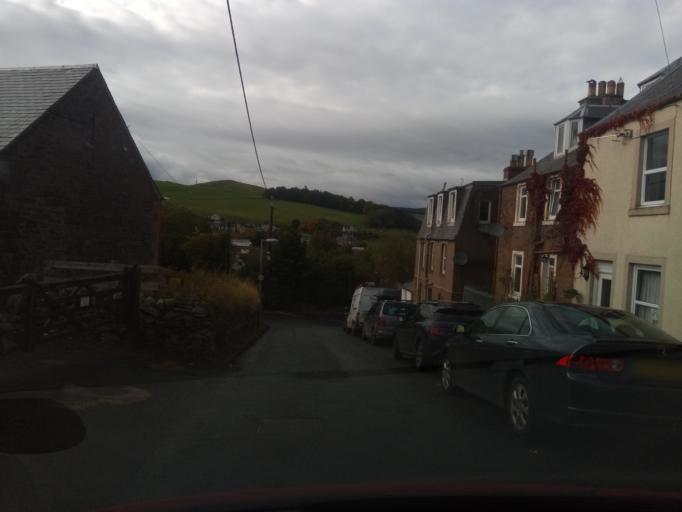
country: GB
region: Scotland
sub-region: The Scottish Borders
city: Galashiels
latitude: 55.6966
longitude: -2.8665
